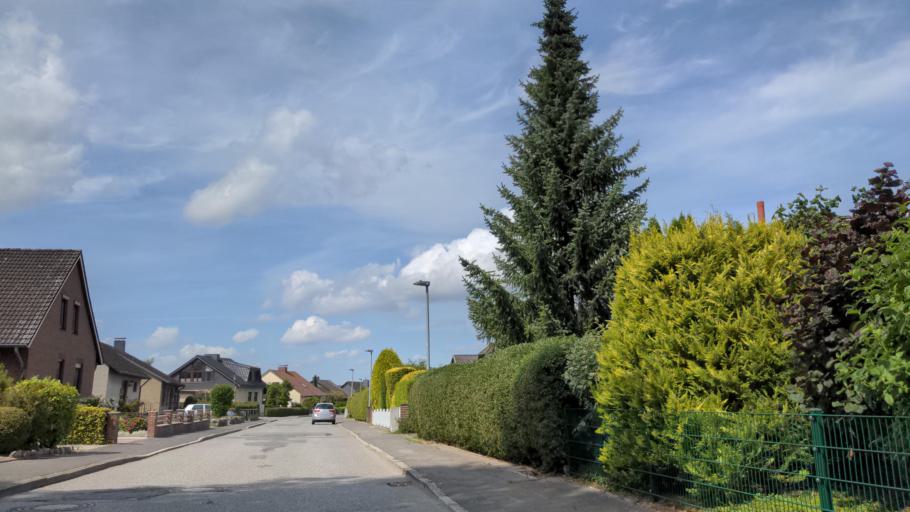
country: DE
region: Schleswig-Holstein
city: Eutin
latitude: 54.1233
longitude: 10.6073
